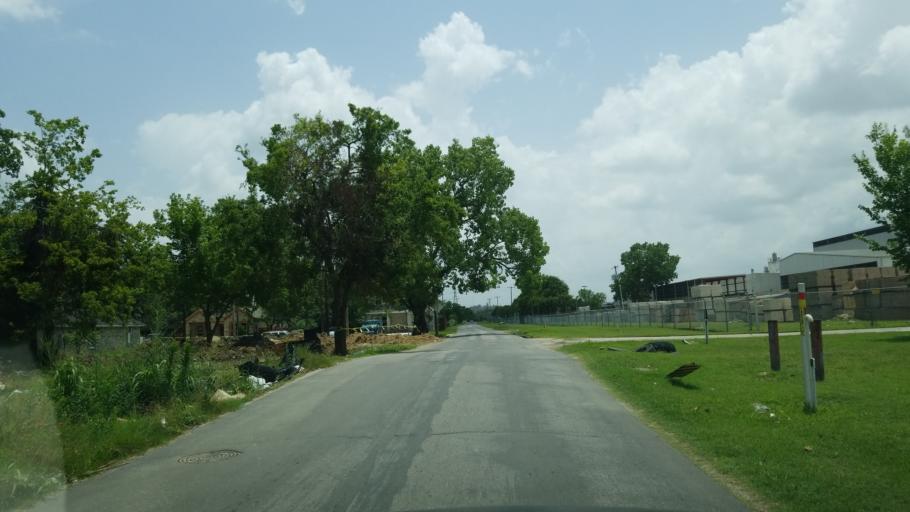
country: US
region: Texas
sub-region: Dallas County
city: Cockrell Hill
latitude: 32.7835
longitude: -96.8826
